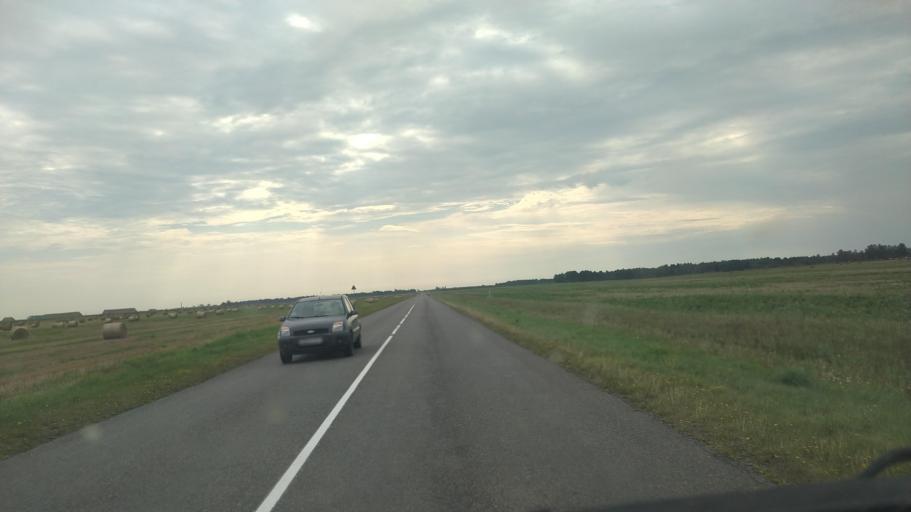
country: BY
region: Brest
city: Byaroza
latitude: 52.5759
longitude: 24.8725
